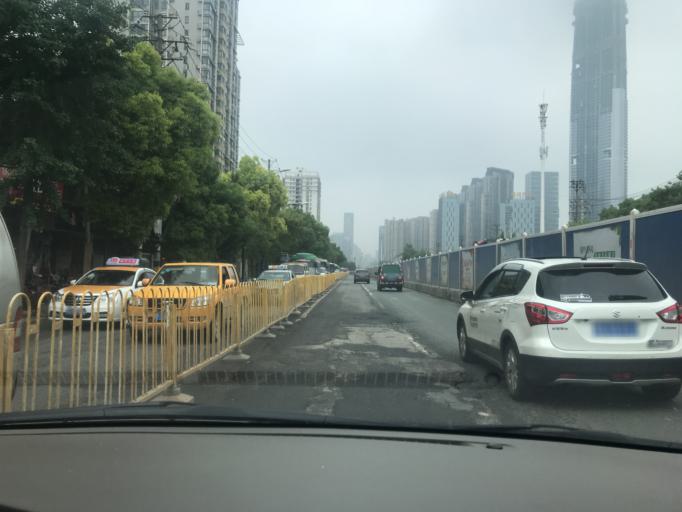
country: CN
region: Hubei
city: Jiang'an
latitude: 30.5900
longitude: 114.3254
